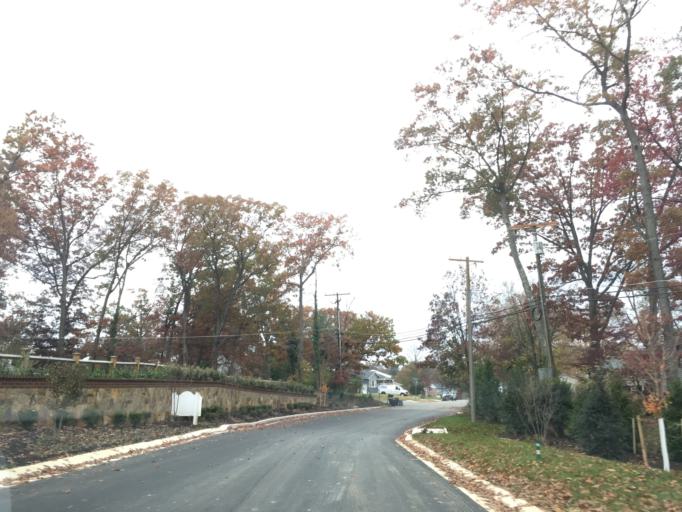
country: US
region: Maryland
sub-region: Baltimore County
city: Timonium
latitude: 39.4285
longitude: -76.6076
